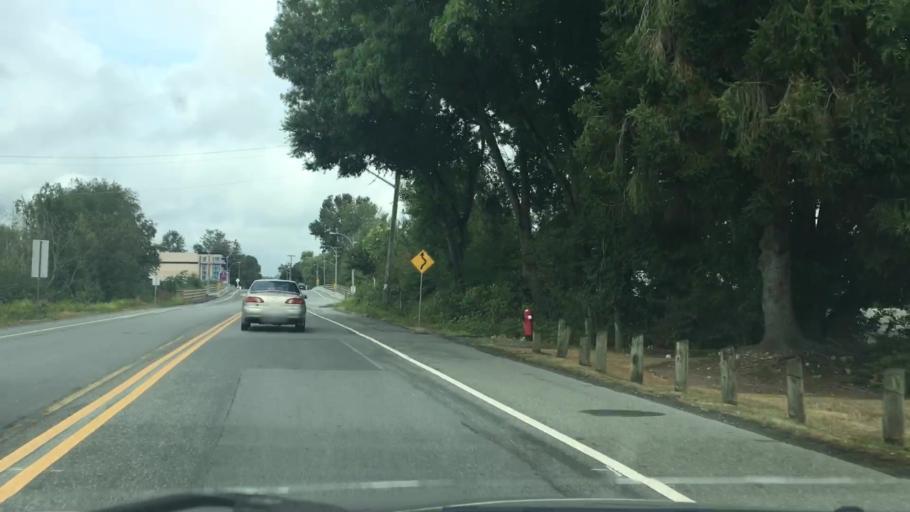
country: CA
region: British Columbia
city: Langley
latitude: 49.1045
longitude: -122.6348
